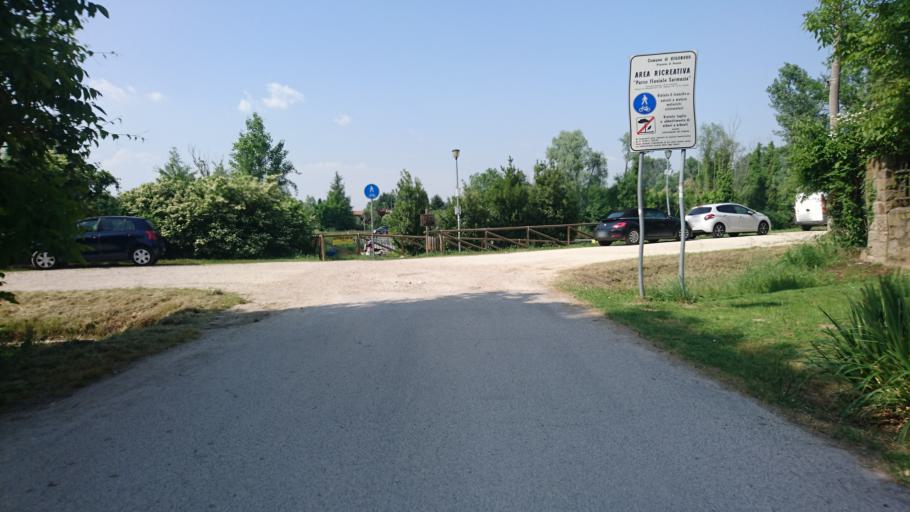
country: IT
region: Veneto
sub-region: Provincia di Venezia
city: Vigonovo
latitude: 45.3932
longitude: 12.0036
